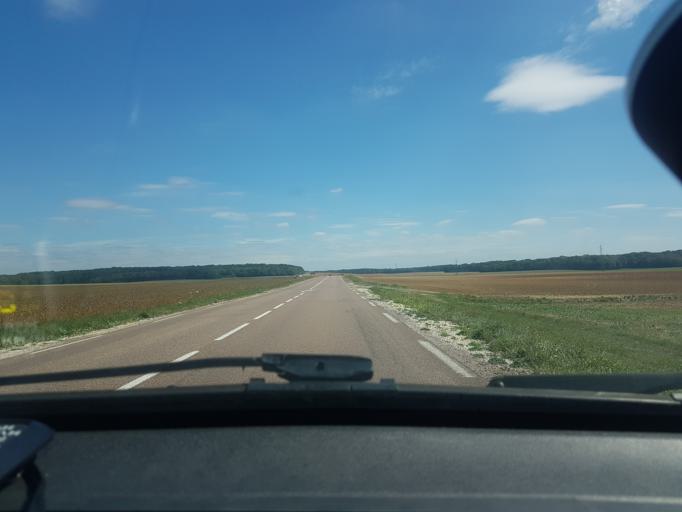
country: FR
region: Bourgogne
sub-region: Departement de la Cote-d'Or
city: Pontailler-sur-Saone
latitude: 47.3983
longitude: 5.4306
